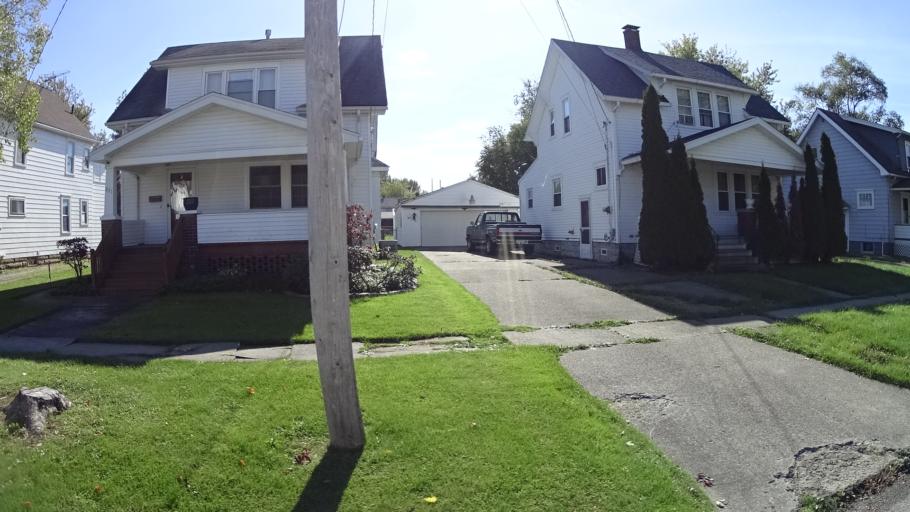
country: US
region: Ohio
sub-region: Lorain County
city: Lorain
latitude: 41.4538
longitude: -82.1766
